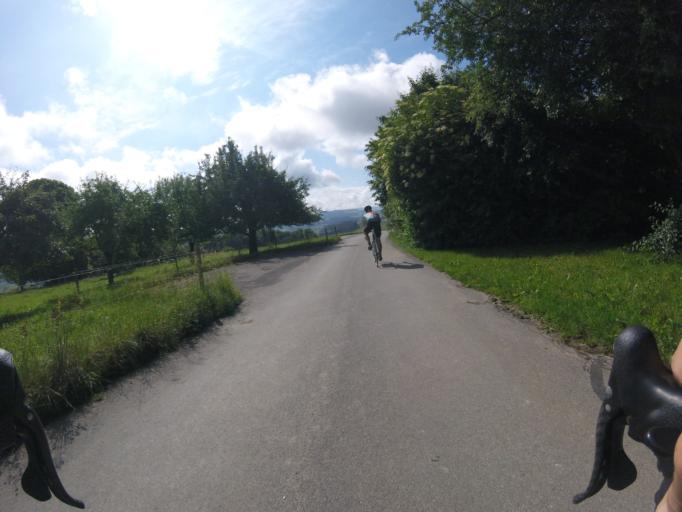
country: CH
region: Bern
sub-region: Bern-Mittelland District
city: Vechigen
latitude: 46.9374
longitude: 7.5404
